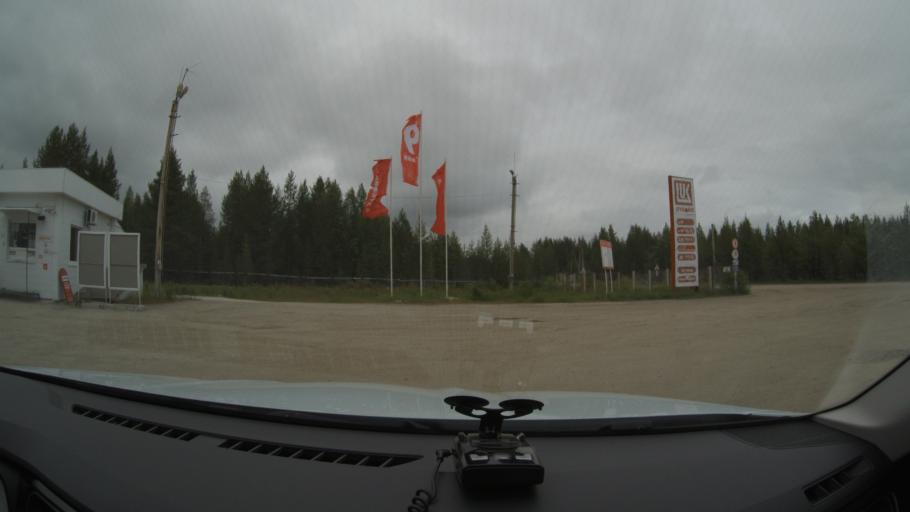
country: RU
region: Komi Republic
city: Kozhva
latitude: 65.1166
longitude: 56.9995
